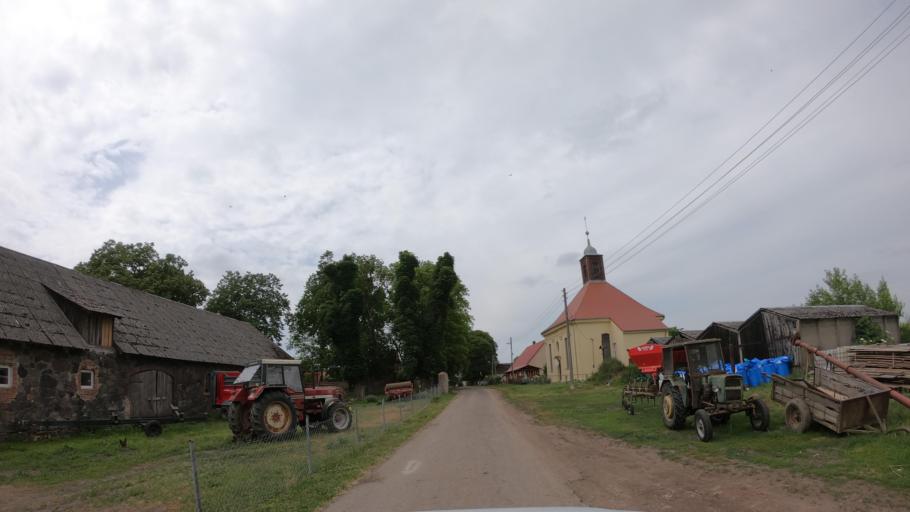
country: PL
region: West Pomeranian Voivodeship
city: Trzcinsko Zdroj
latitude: 52.9462
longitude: 14.7260
